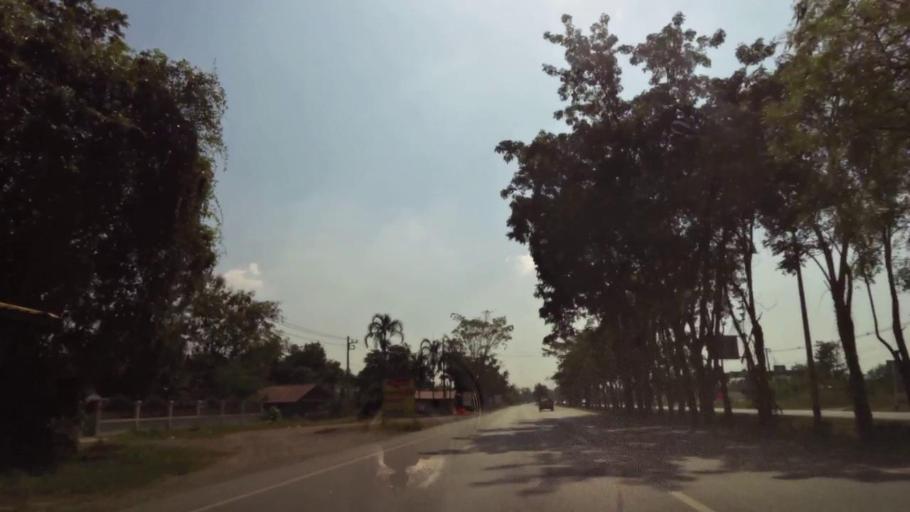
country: TH
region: Phichit
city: Bueng Na Rang
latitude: 16.1883
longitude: 100.1288
